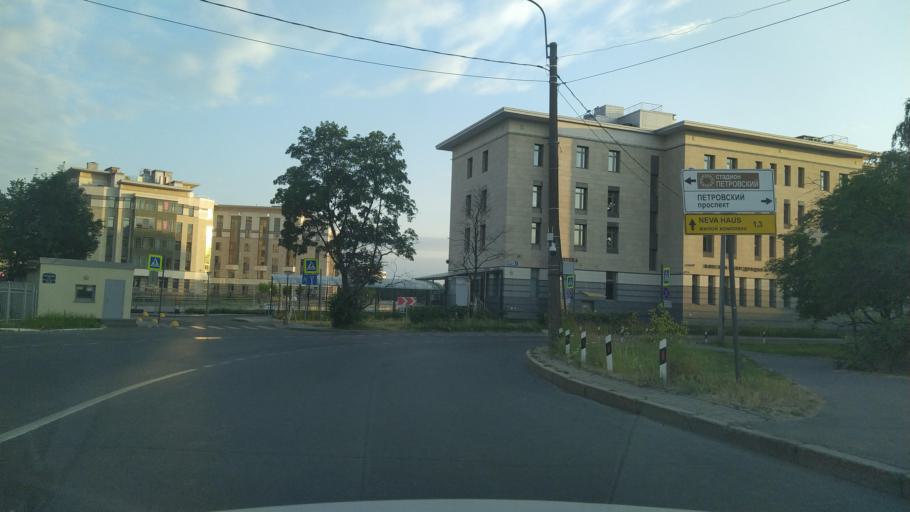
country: RU
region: Leningrad
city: Krestovskiy ostrov
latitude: 59.9549
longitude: 30.2805
